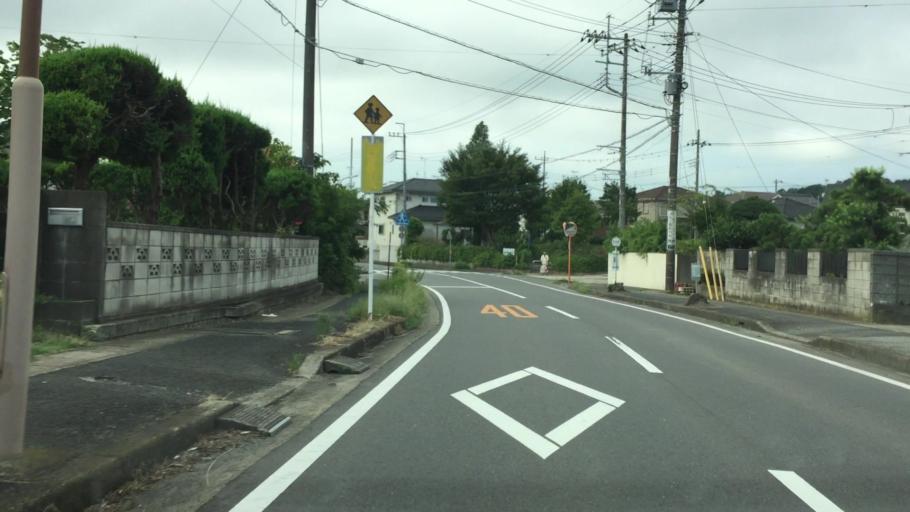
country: JP
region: Ibaraki
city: Ryugasaki
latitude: 35.8605
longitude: 140.1507
